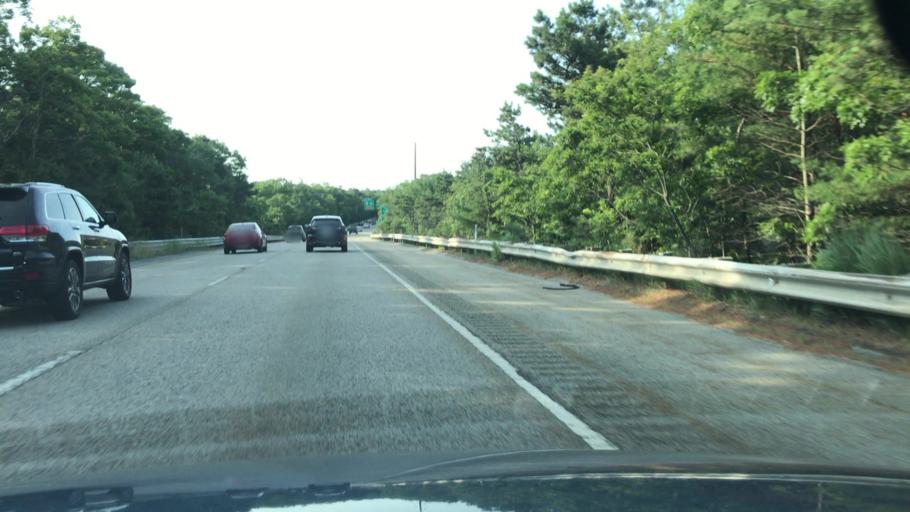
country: US
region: Massachusetts
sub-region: Barnstable County
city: Sagamore
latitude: 41.8040
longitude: -70.5486
